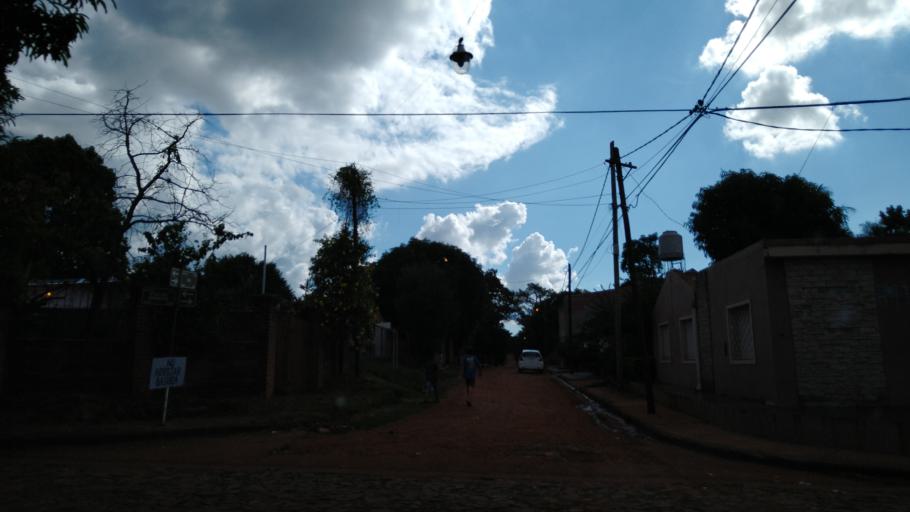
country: AR
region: Misiones
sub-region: Departamento de Capital
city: Posadas
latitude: -27.4113
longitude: -55.9048
